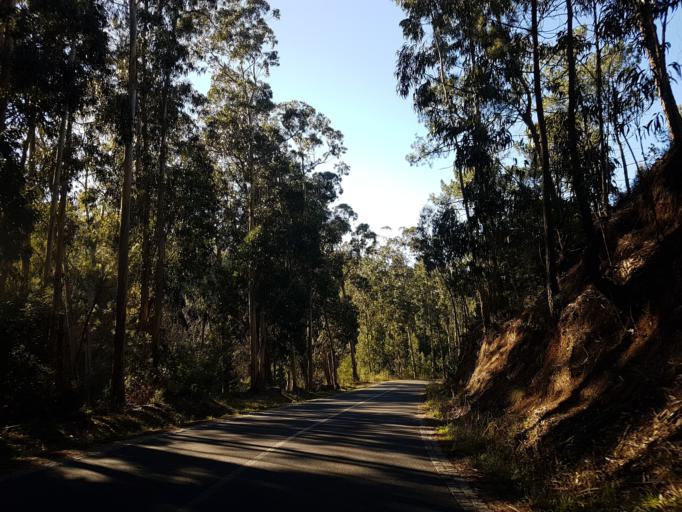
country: PT
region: Lisbon
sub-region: Cascais
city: Alcabideche
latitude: 38.7591
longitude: -9.4126
